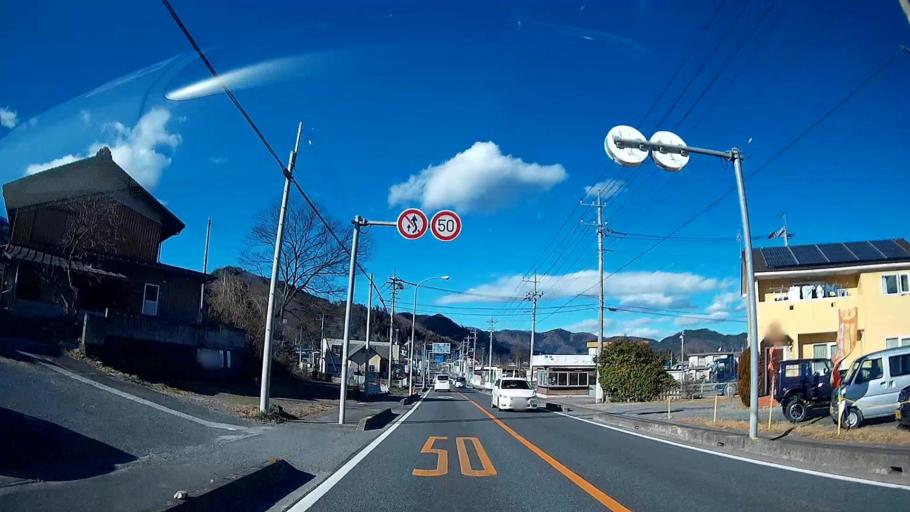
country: JP
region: Saitama
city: Yorii
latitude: 36.0917
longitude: 139.1125
